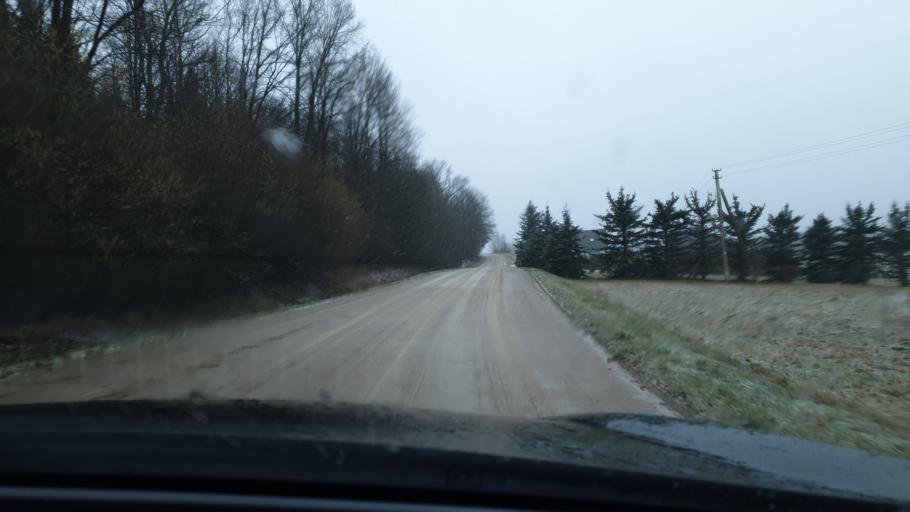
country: LT
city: Jieznas
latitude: 54.5677
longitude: 24.3186
